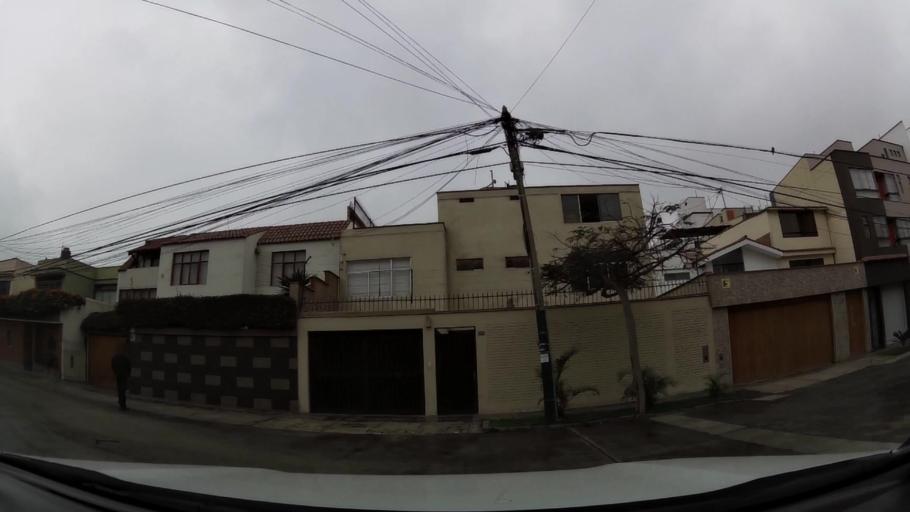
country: PE
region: Lima
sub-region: Lima
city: Surco
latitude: -12.1338
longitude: -77.0010
